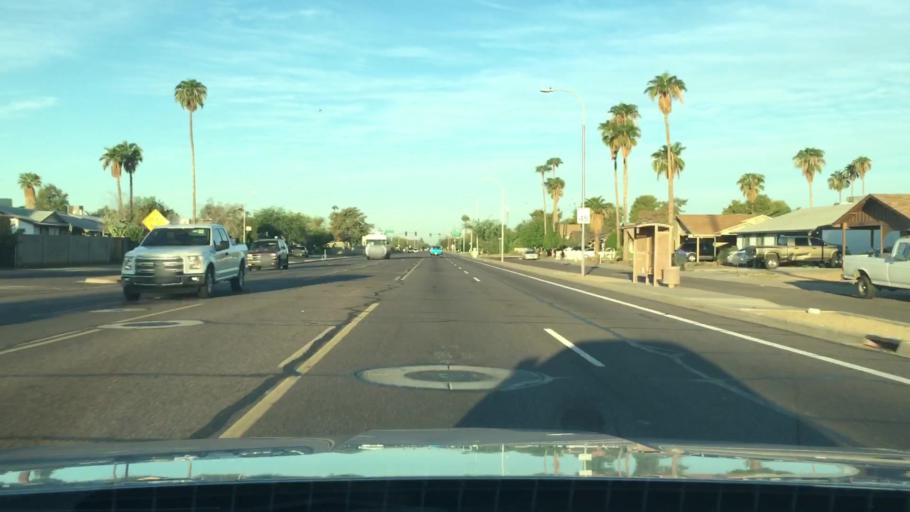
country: US
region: Arizona
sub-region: Maricopa County
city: Guadalupe
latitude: 33.3928
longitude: -111.9829
